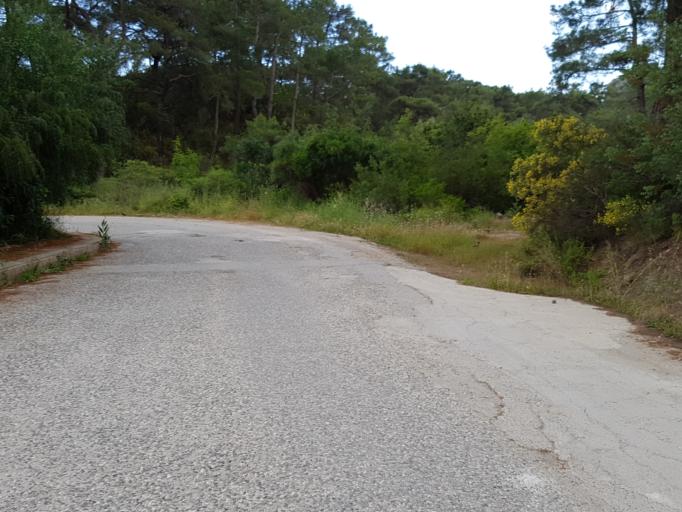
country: TR
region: Antalya
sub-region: Kemer
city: Goeynuek
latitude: 36.6440
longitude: 30.5487
